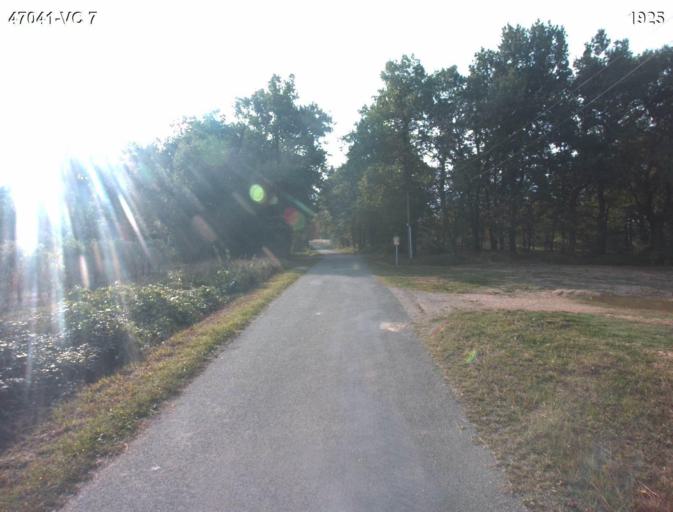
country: FR
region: Aquitaine
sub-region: Departement du Lot-et-Garonne
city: Port-Sainte-Marie
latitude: 44.1937
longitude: 0.4200
